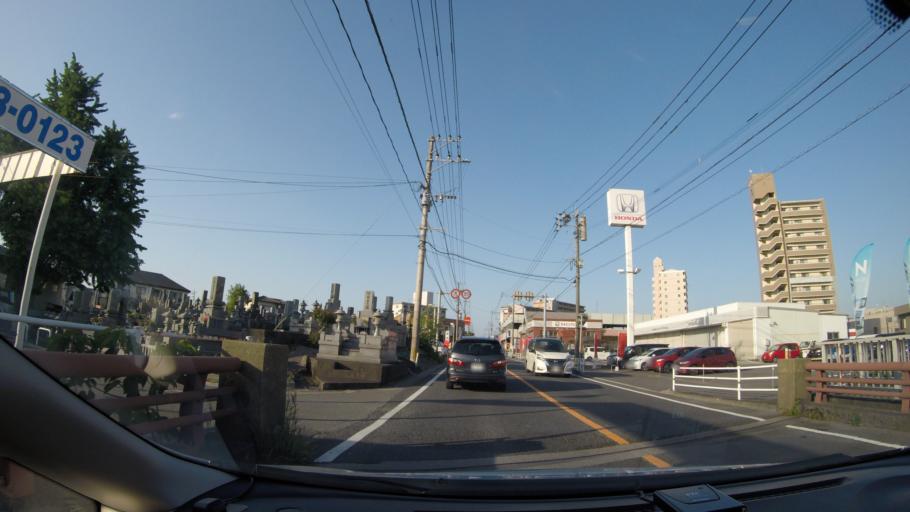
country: JP
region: Oita
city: Oita
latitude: 33.2079
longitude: 131.6043
